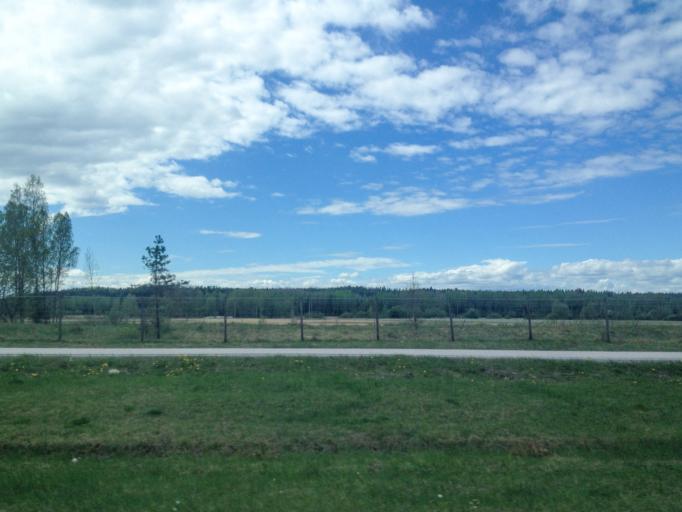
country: FI
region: Uusimaa
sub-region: Helsinki
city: Hyvinge
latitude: 60.6414
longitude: 24.8088
